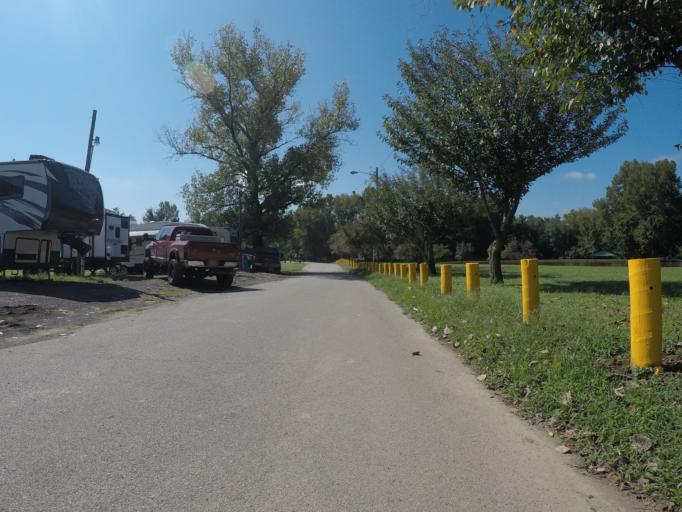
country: US
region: Ohio
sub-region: Lawrence County
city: South Point
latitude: 38.4138
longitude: -82.5937
